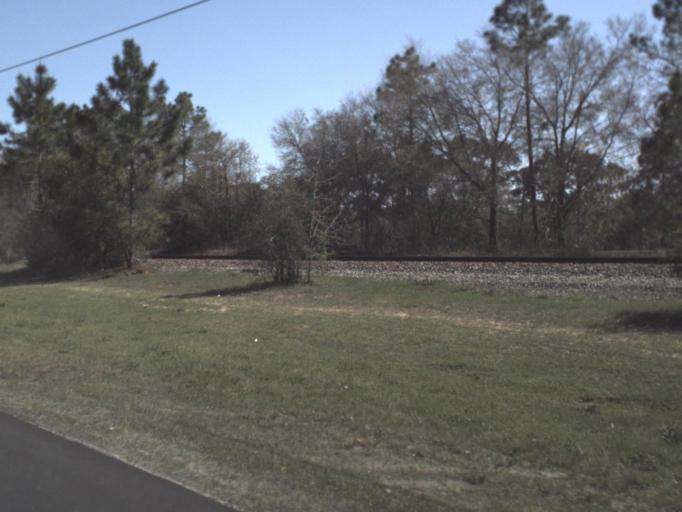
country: US
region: Florida
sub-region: Walton County
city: DeFuniak Springs
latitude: 30.7322
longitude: -86.1424
